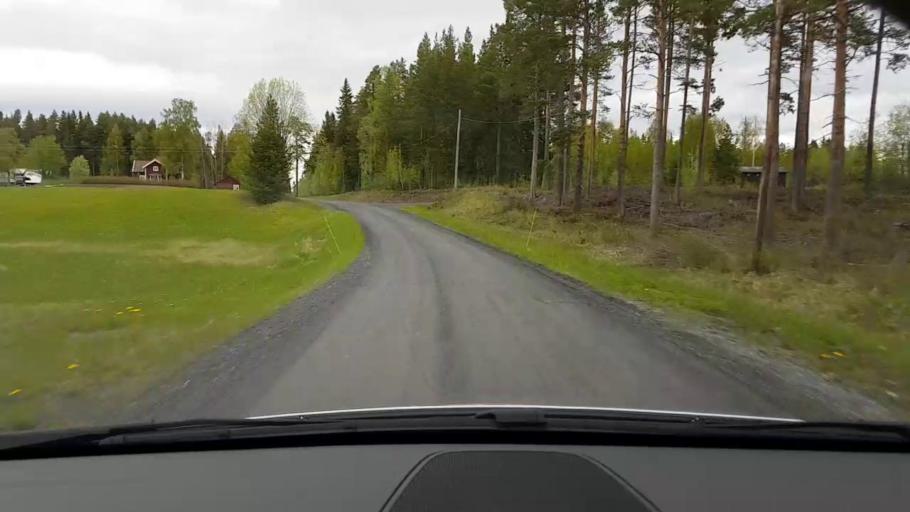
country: SE
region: Jaemtland
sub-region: Krokoms Kommun
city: Krokom
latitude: 63.2938
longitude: 14.3919
